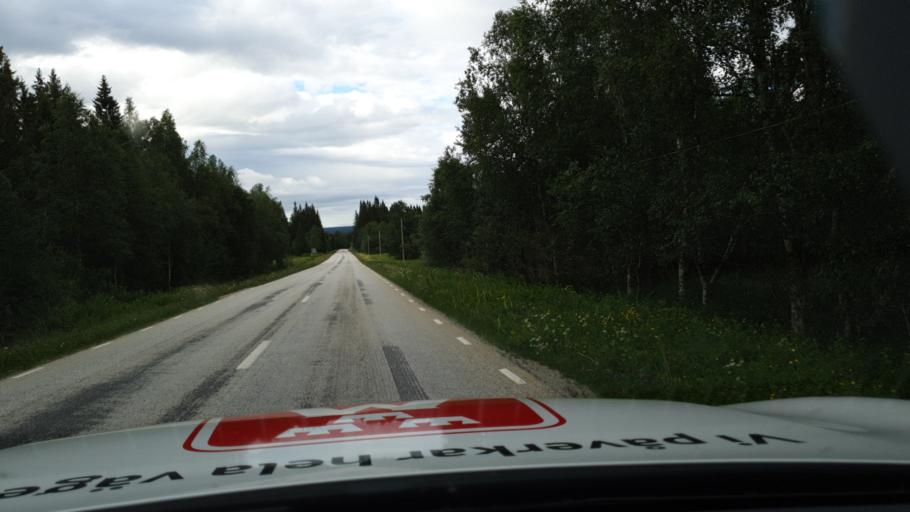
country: SE
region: Jaemtland
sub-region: Bergs Kommun
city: Hoverberg
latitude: 62.5932
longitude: 14.3113
